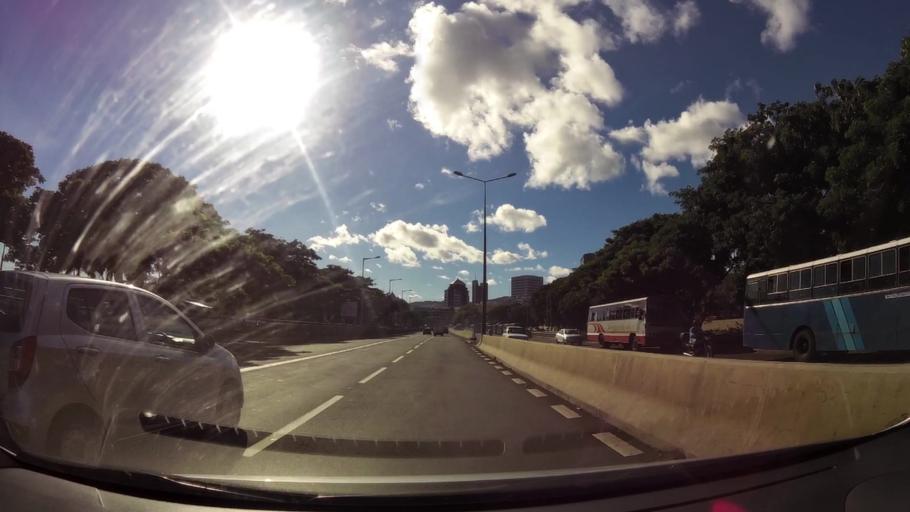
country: MU
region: Port Louis
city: Port Louis
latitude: -20.1636
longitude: 57.4951
